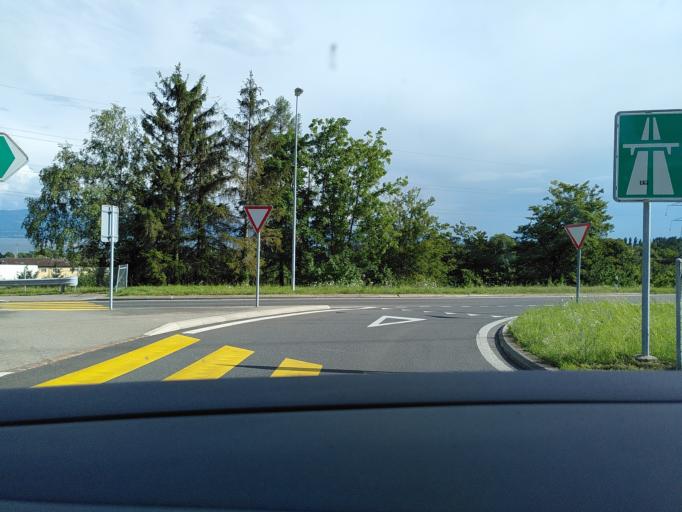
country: CH
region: Vaud
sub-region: Nyon District
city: Rolle
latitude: 46.4655
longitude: 6.3326
